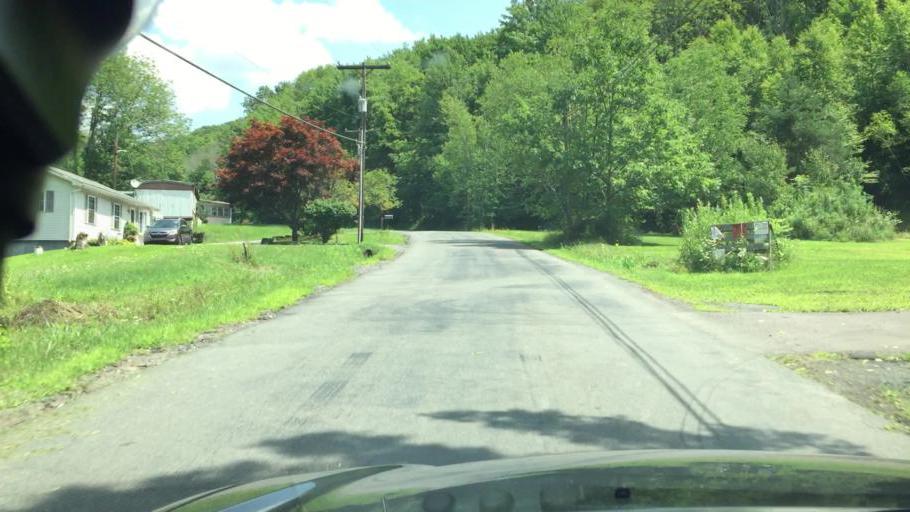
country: US
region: Pennsylvania
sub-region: Luzerne County
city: Oakdale
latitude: 41.0139
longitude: -75.9462
